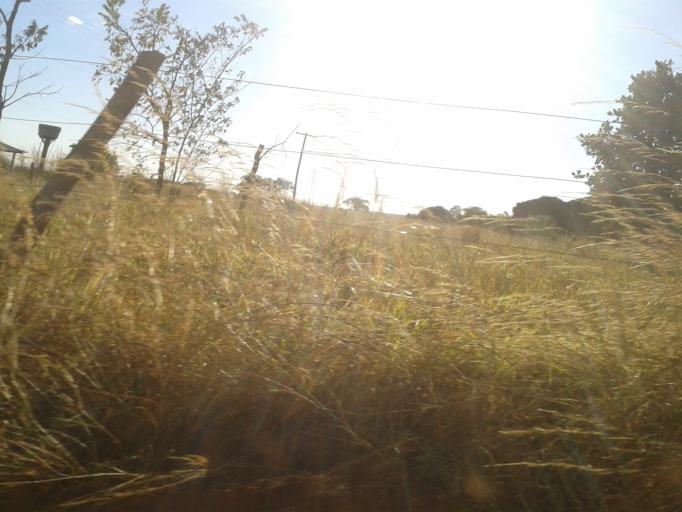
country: BR
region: Minas Gerais
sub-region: Centralina
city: Centralina
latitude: -18.7455
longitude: -49.0923
